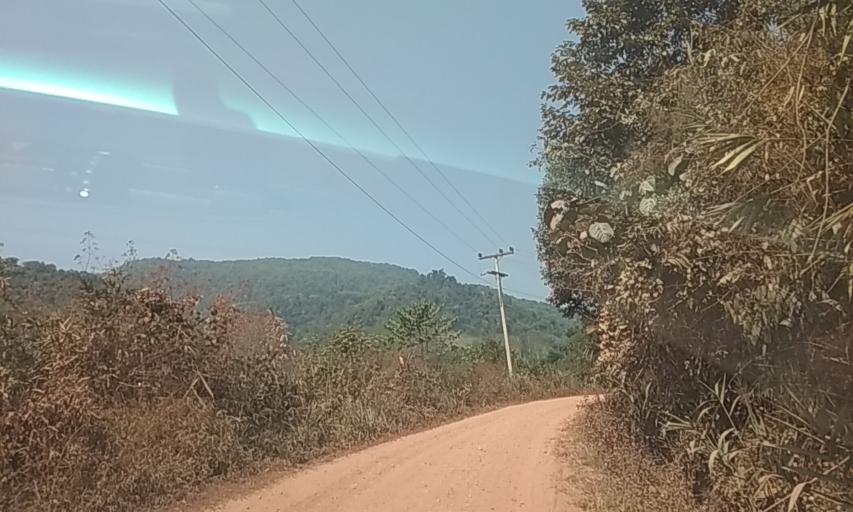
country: CN
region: Yunnan
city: Mengla
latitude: 21.5298
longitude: 101.8306
